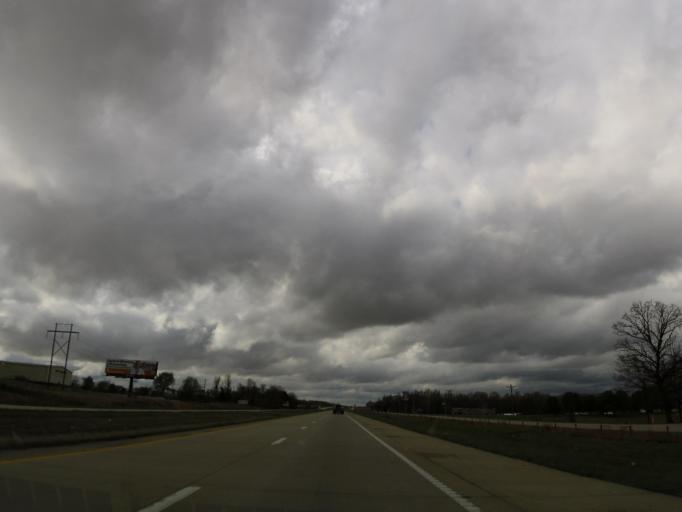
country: US
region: Missouri
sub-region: Butler County
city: Poplar Bluff
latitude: 36.7233
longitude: -90.4646
